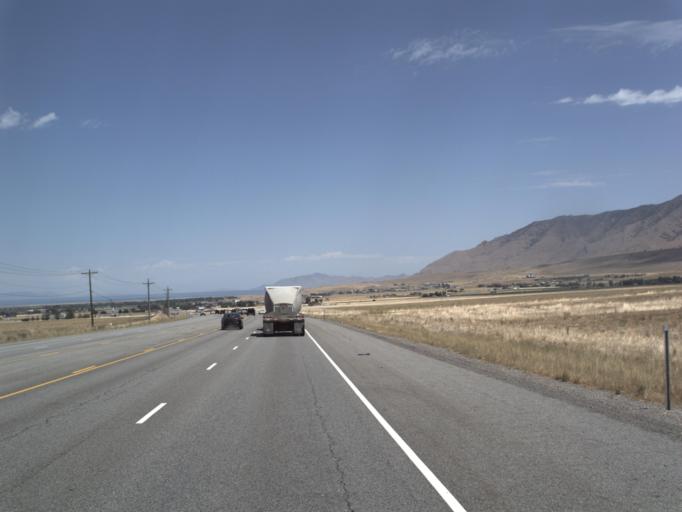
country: US
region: Utah
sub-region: Tooele County
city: Erda
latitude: 40.5750
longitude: -112.2946
